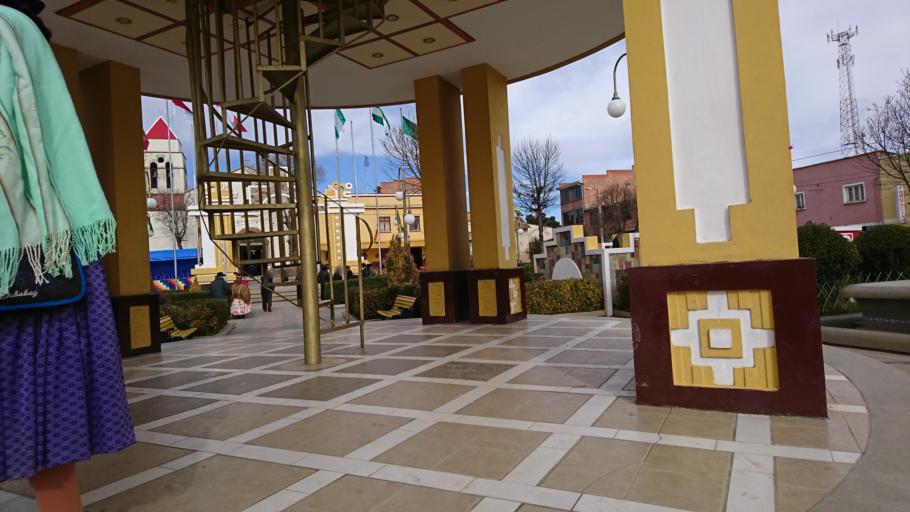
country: BO
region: La Paz
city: Batallas
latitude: -16.3997
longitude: -68.4775
